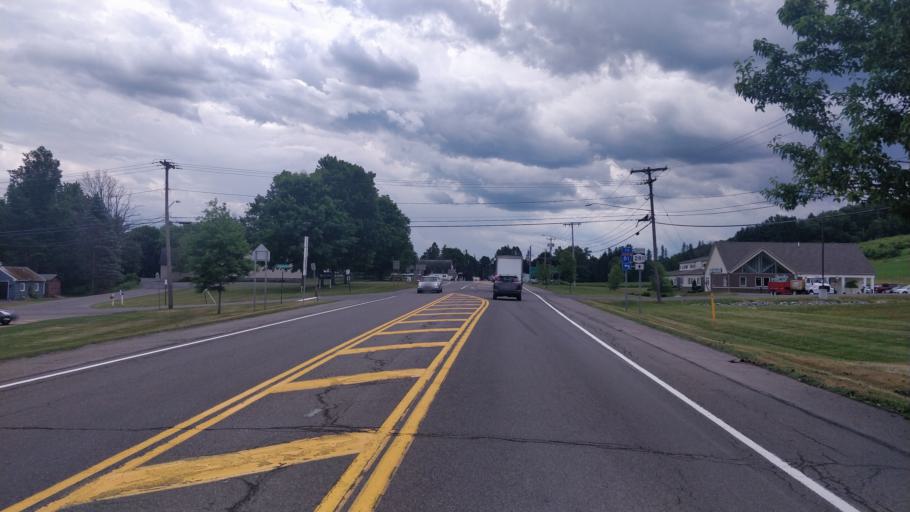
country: US
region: New York
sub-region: Cortland County
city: Homer
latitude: 42.6297
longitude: -76.1917
